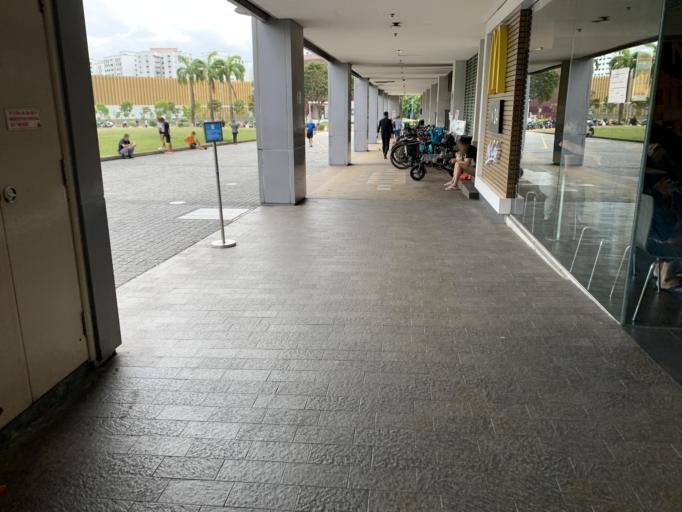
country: MY
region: Johor
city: Johor Bahru
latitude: 1.4367
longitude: 103.7866
